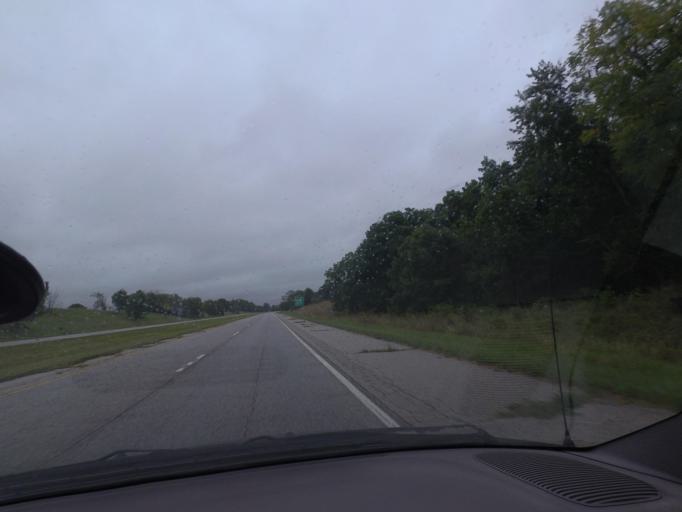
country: US
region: Illinois
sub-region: Pike County
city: Pittsfield
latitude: 39.6728
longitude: -90.7858
